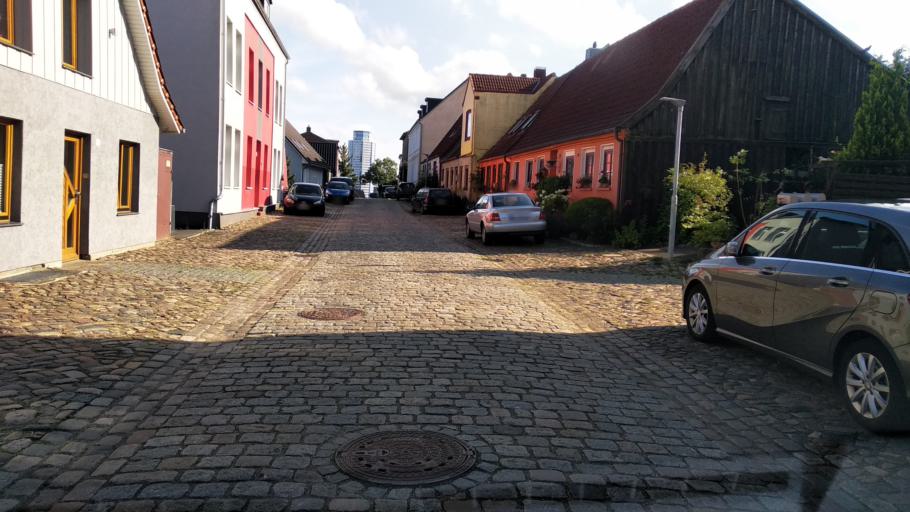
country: DE
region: Schleswig-Holstein
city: Schleswig
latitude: 54.5150
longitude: 9.5483
